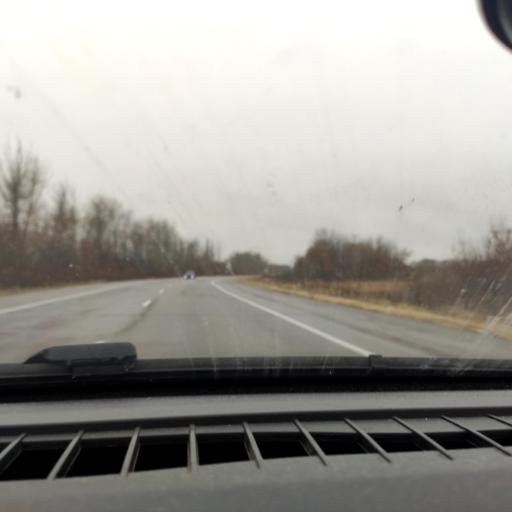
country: RU
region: Voronezj
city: Kolodeznyy
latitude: 51.2866
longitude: 39.0409
